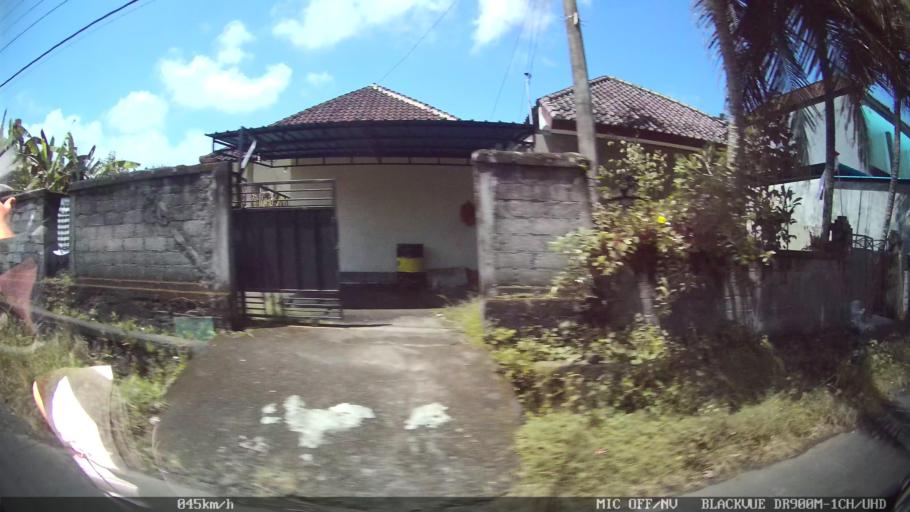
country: ID
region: Bali
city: Banjar Kelodan
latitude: -8.5288
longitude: 115.3357
